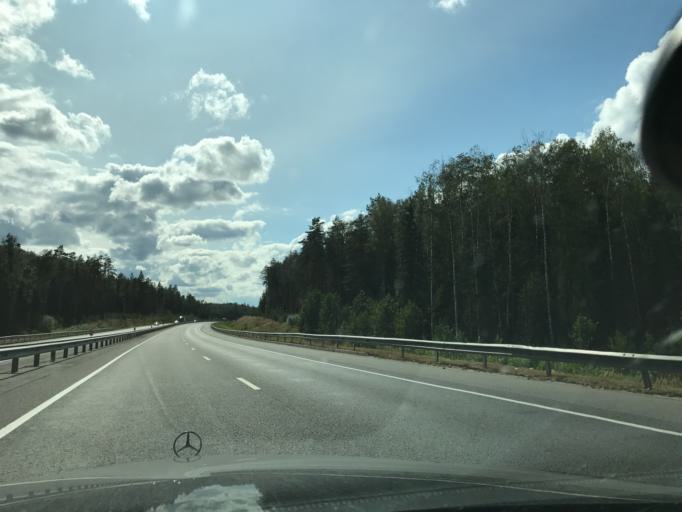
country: RU
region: Vladimir
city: Sudogda
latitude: 56.1503
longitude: 40.9171
